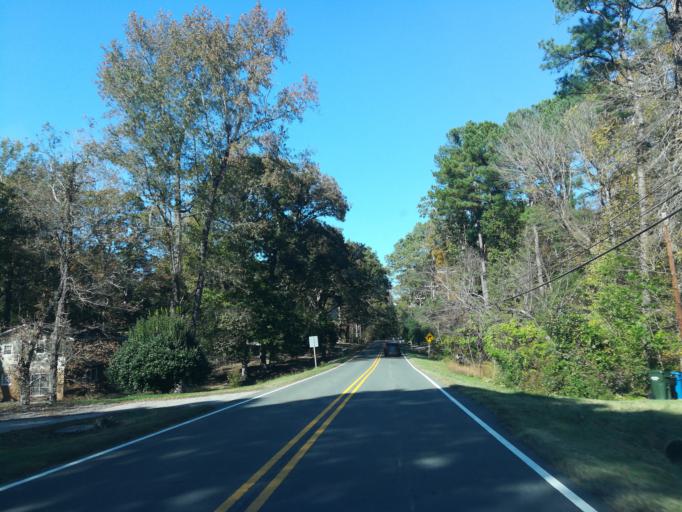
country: US
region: North Carolina
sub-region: Durham County
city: Durham
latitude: 36.0434
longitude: -78.9819
